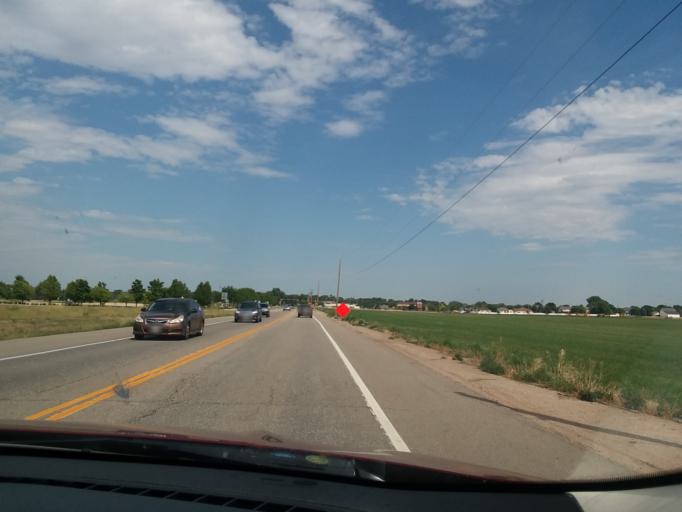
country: US
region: Colorado
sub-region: Larimer County
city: Berthoud
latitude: 40.3051
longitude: -105.0998
